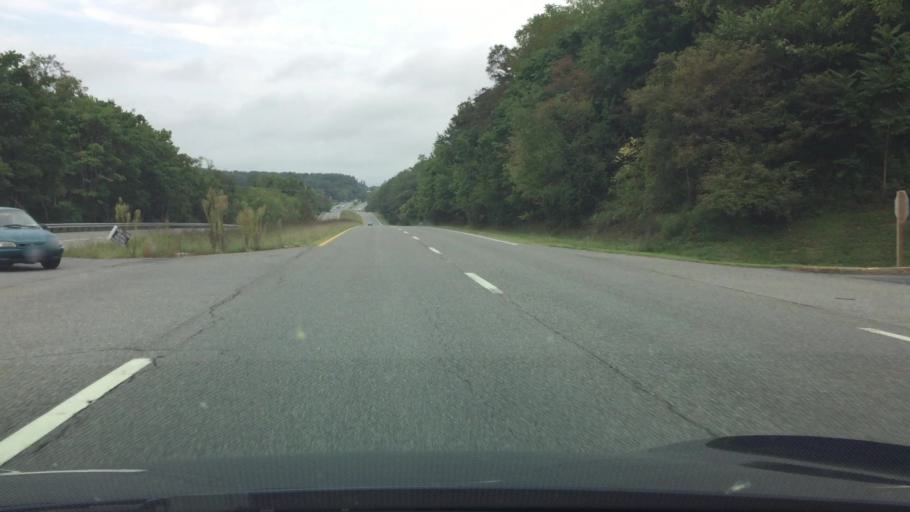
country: US
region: Virginia
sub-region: City of Radford
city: Radford
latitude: 37.1122
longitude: -80.5247
